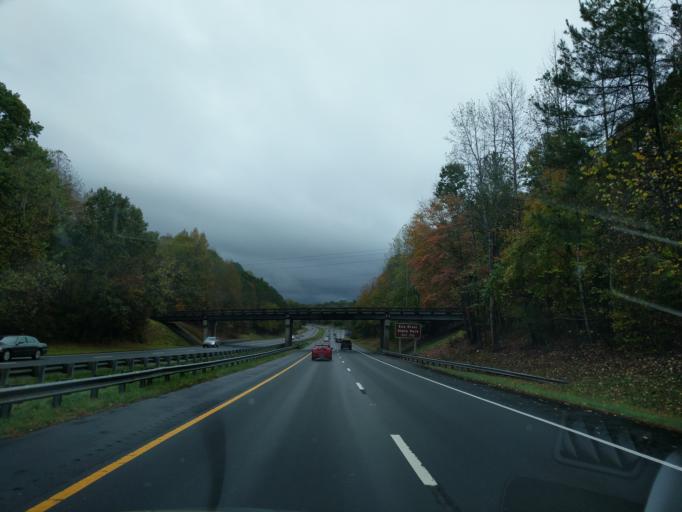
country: US
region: North Carolina
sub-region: Orange County
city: Hillsborough
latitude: 36.0420
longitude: -79.0332
